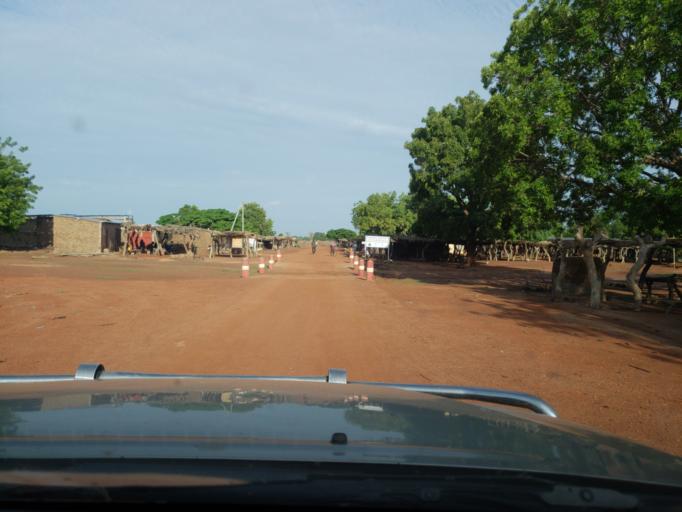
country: ML
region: Sikasso
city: Koutiala
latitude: 12.4224
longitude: -5.6856
